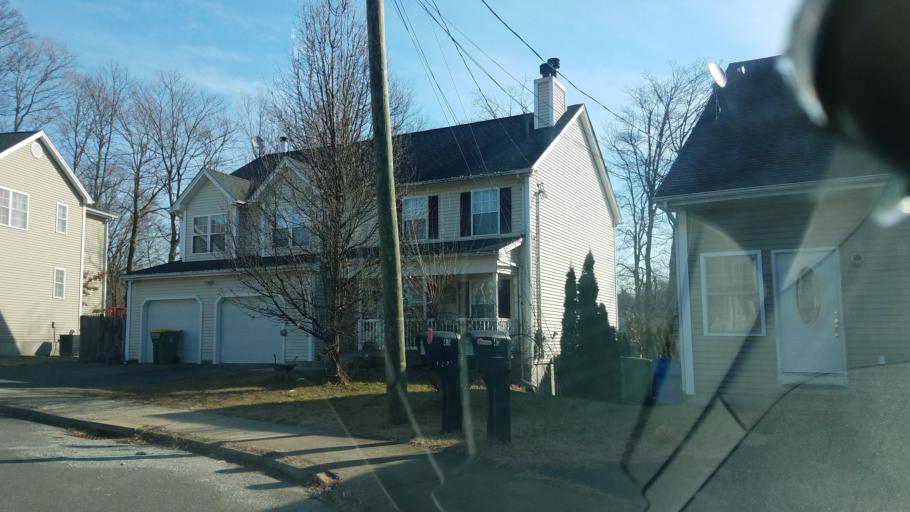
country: US
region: Connecticut
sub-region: New Haven County
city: Wolcott
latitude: 41.5537
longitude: -72.9875
